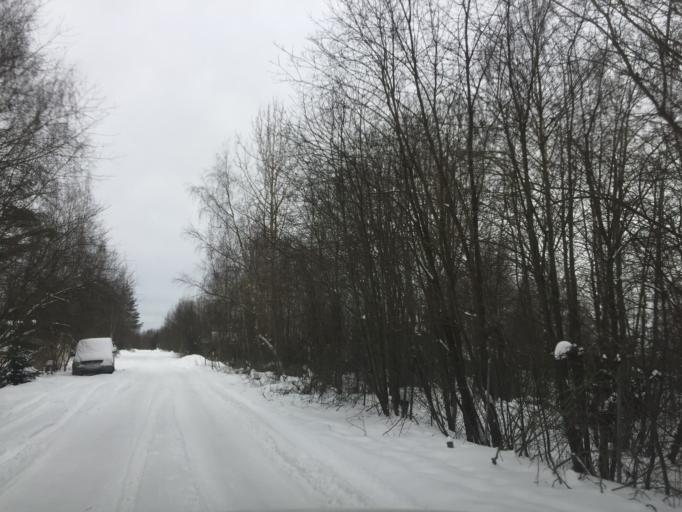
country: RU
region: Leningrad
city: Otradnoye
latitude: 59.7868
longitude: 30.7891
